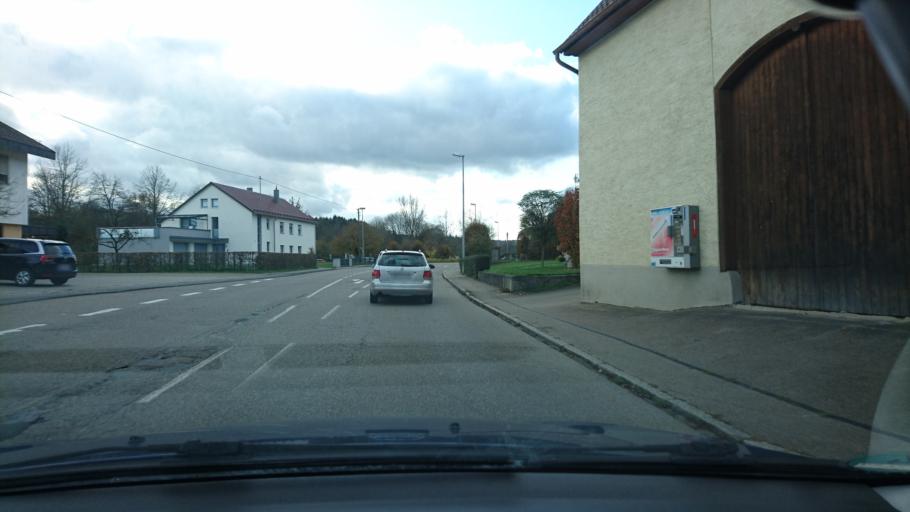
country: DE
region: Baden-Wuerttemberg
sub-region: Regierungsbezirk Stuttgart
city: Heuchlingen
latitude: 48.8523
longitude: 9.9424
